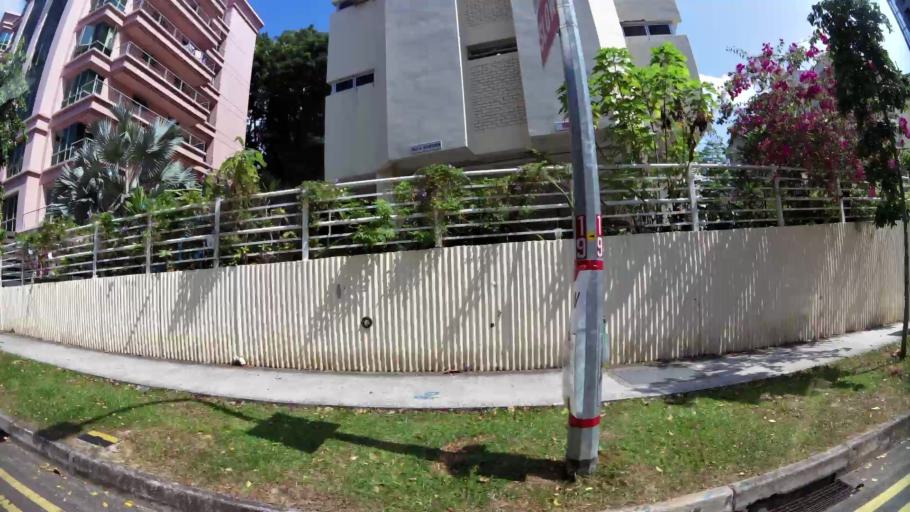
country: SG
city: Singapore
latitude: 1.3023
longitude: 103.8485
